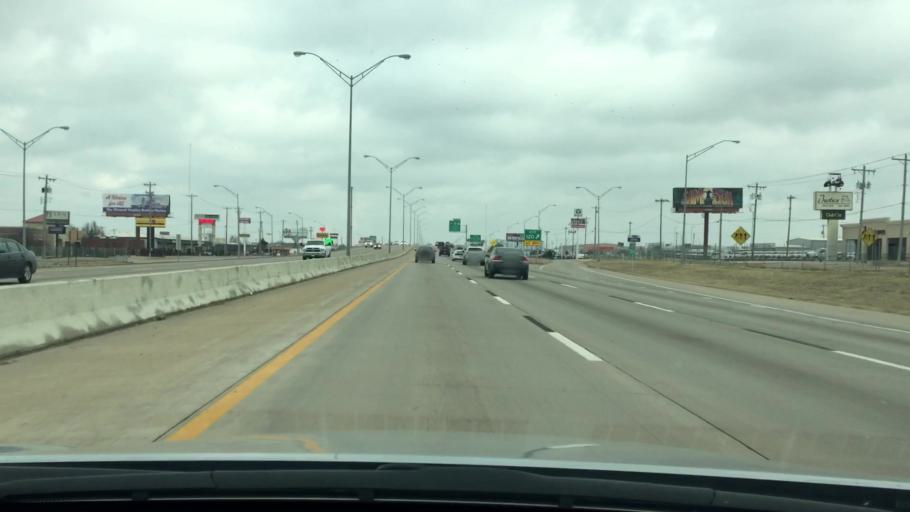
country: US
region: Oklahoma
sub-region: Cleveland County
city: Moore
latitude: 35.3736
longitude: -97.4949
